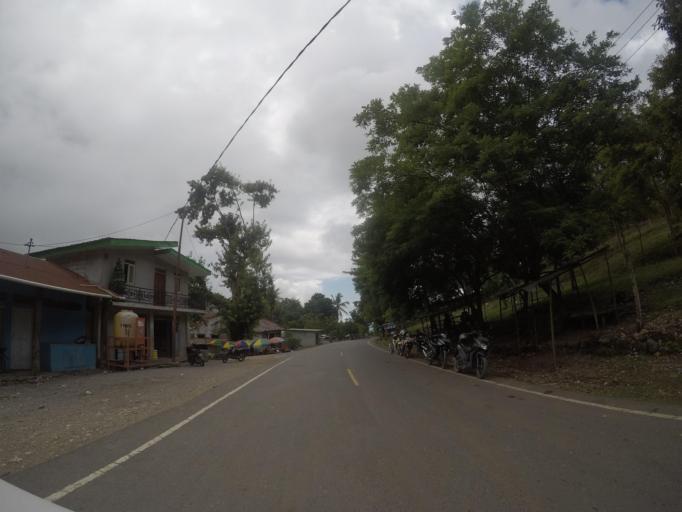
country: TL
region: Bobonaro
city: Maliana
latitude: -8.9694
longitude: 125.0428
